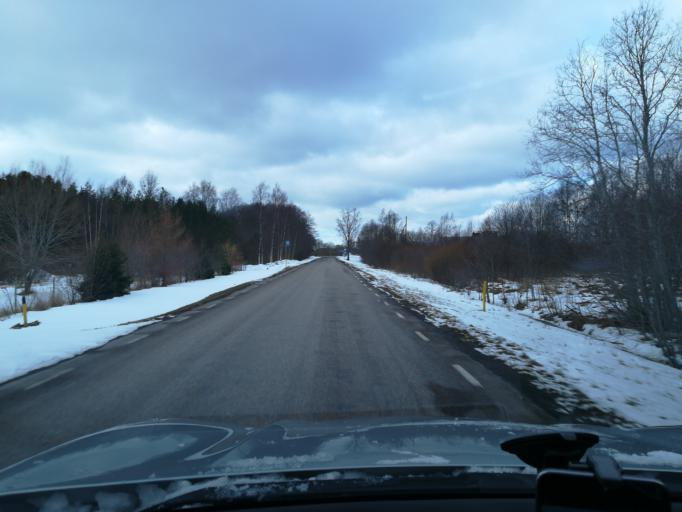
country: EE
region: Harju
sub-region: Keila linn
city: Keila
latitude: 59.4442
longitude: 24.3837
